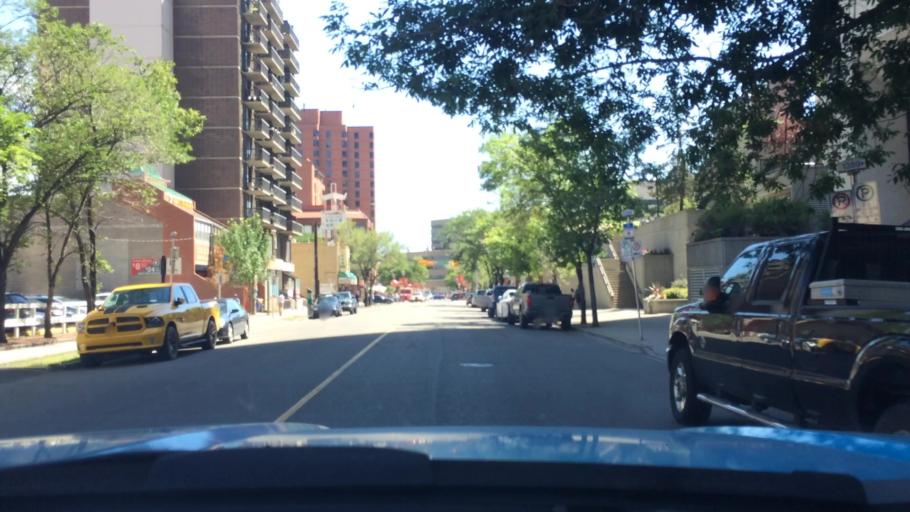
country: CA
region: Alberta
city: Calgary
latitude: 51.0504
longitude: -114.0646
